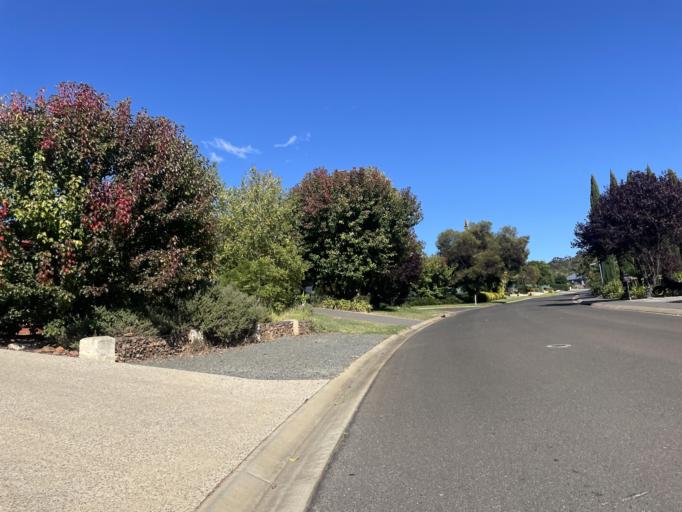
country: AU
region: South Australia
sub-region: Clare and Gilbert Valleys
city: Clare
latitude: -33.8448
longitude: 138.6121
